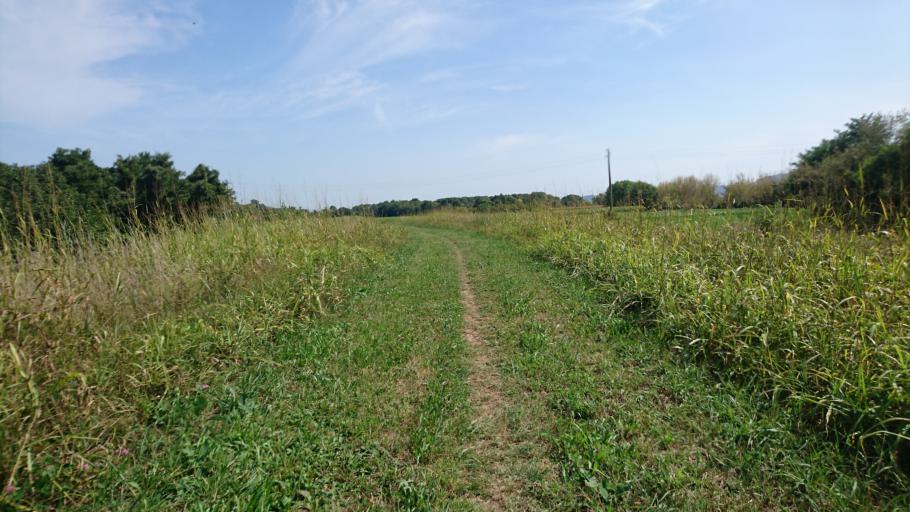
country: IT
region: Veneto
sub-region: Provincia di Vicenza
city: Montegalda
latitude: 45.4524
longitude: 11.6565
